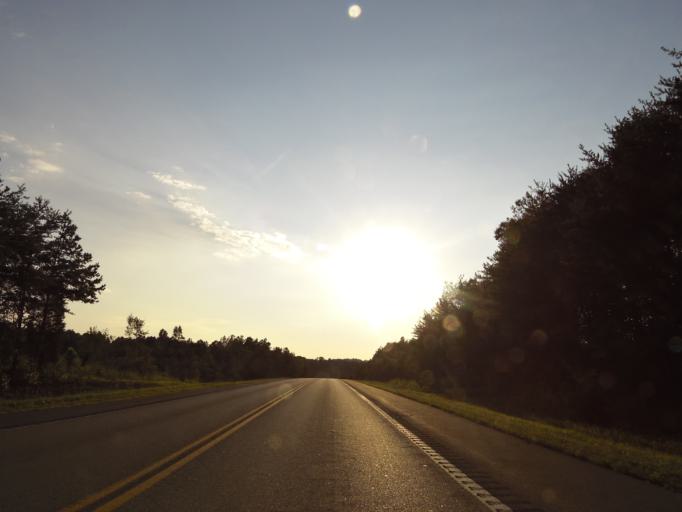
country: US
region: Tennessee
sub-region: McMinn County
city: Athens
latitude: 35.5207
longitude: -84.6411
